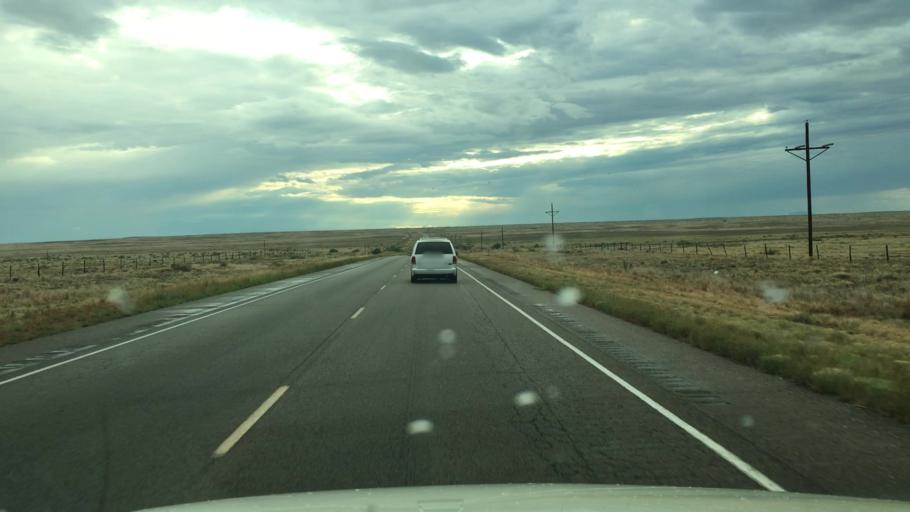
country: US
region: New Mexico
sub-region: Chaves County
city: Dexter
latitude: 33.4073
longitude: -104.2948
